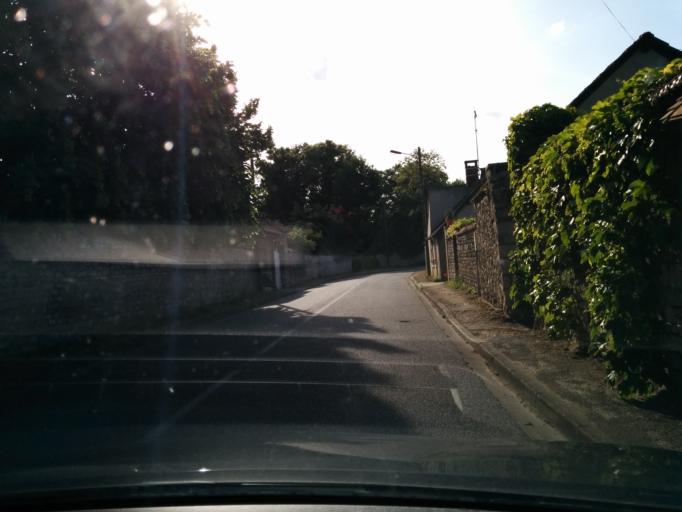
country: FR
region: Haute-Normandie
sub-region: Departement de l'Eure
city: Courcelles-sur-Seine
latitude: 49.1714
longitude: 1.4014
